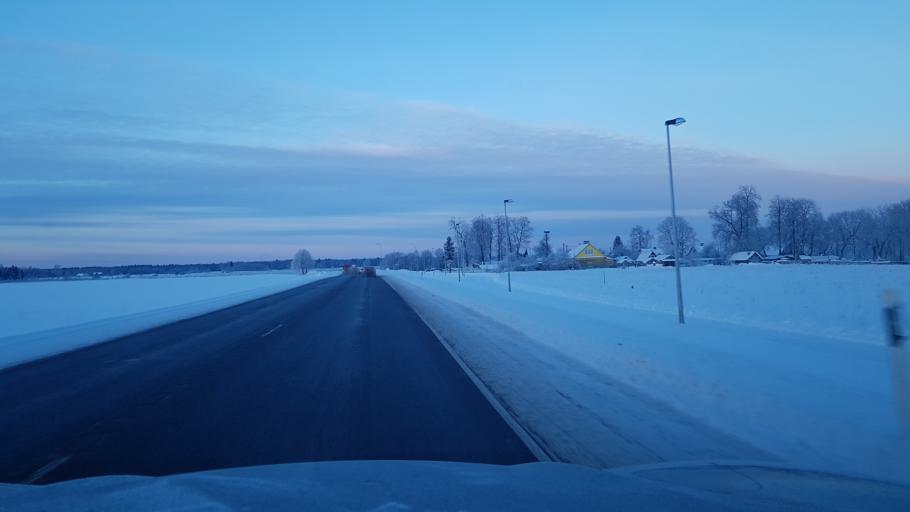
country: EE
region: Ida-Virumaa
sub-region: Narva linn
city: Narva
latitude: 59.3899
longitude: 28.1096
